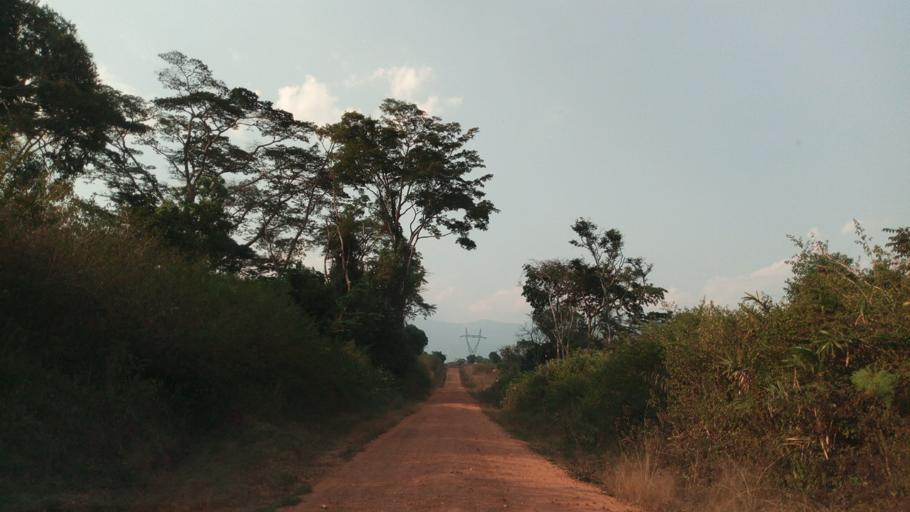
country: TZ
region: Kigoma
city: Kigoma
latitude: -5.1920
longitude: 28.8910
